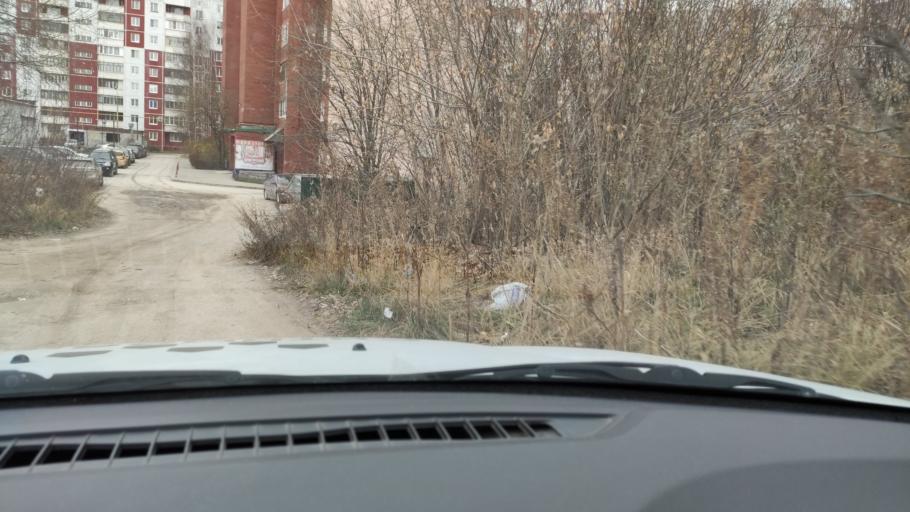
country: RU
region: Perm
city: Perm
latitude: 57.9719
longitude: 56.2670
